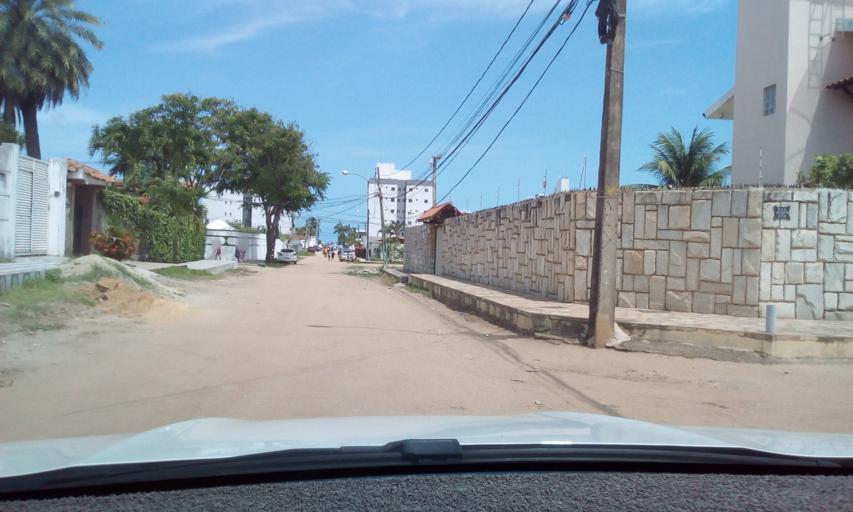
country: BR
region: Paraiba
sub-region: Cabedelo
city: Cabedelo
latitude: -7.0144
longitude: -34.8315
